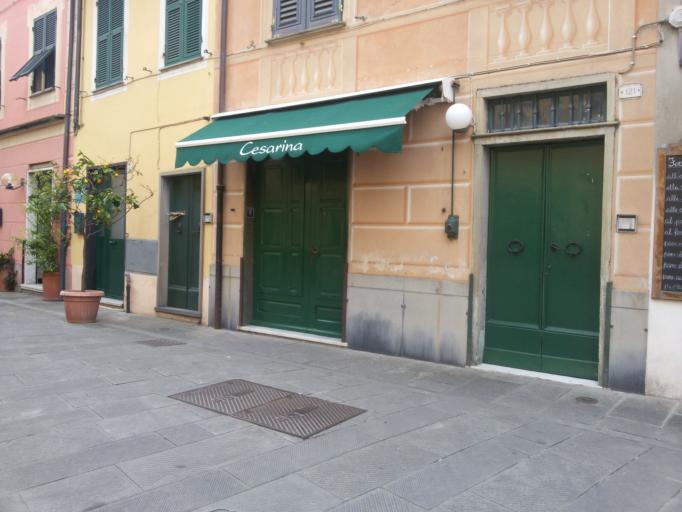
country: IT
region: Liguria
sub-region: Provincia di La Spezia
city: Levanto
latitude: 44.1712
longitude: 9.6135
